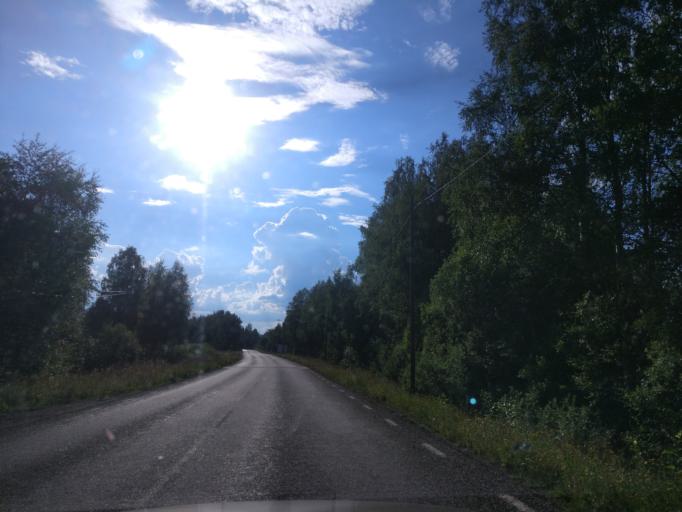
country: SE
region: Dalarna
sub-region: Ludvika Kommun
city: Grangesberg
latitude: 60.2679
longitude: 15.0208
